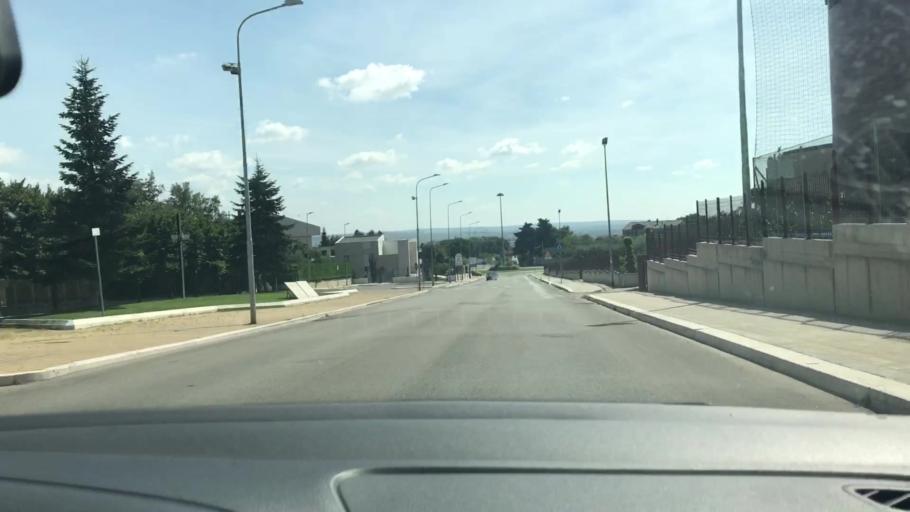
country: IT
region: Apulia
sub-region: Provincia di Bari
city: Altamura
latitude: 40.8261
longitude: 16.5642
